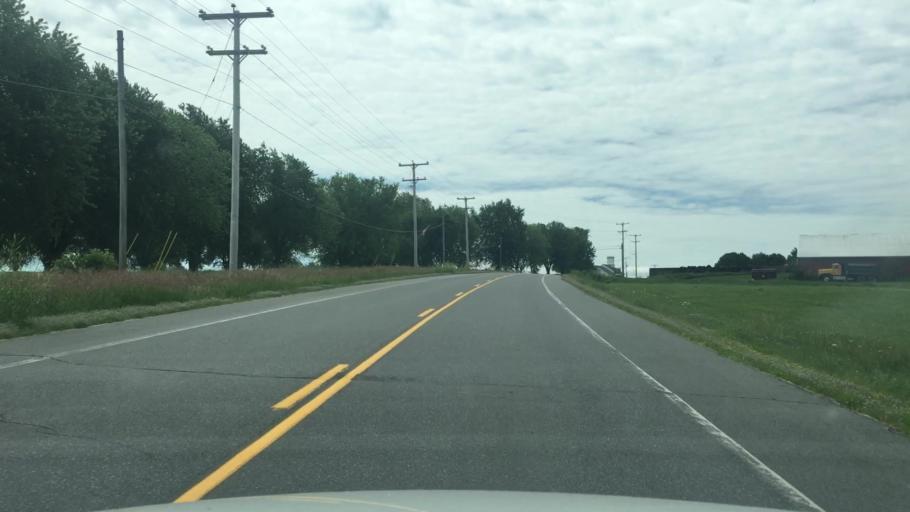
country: US
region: Maine
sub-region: Waldo County
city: Troy
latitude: 44.5434
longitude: -69.2652
